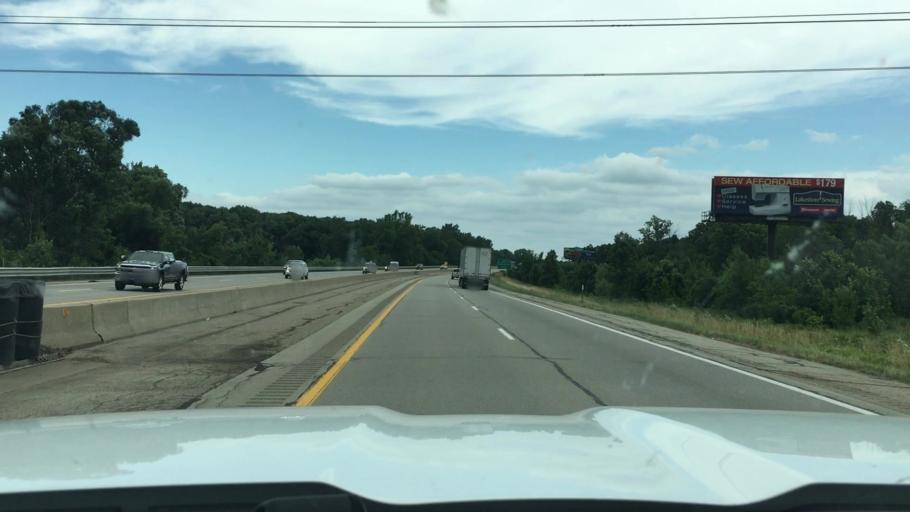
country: US
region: Michigan
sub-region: Kent County
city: Byron Center
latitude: 42.7593
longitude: -85.6736
